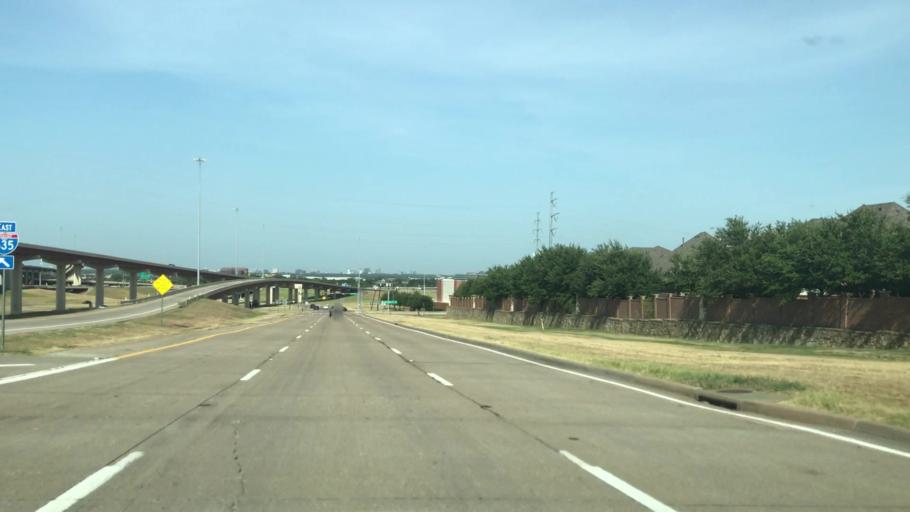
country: US
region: Texas
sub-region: Dallas County
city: Farmers Branch
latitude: 32.9088
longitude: -96.9477
